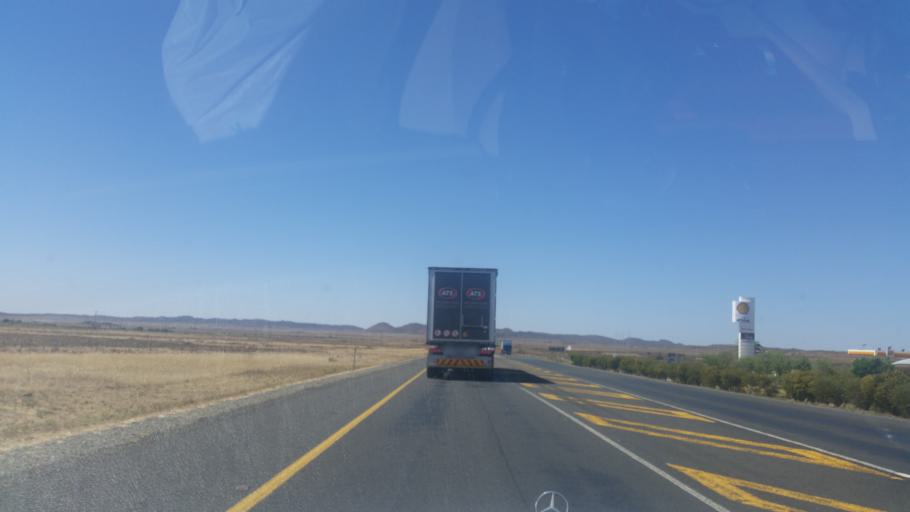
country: ZA
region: Northern Cape
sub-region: Pixley ka Seme District Municipality
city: Colesberg
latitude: -30.7007
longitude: 25.1248
